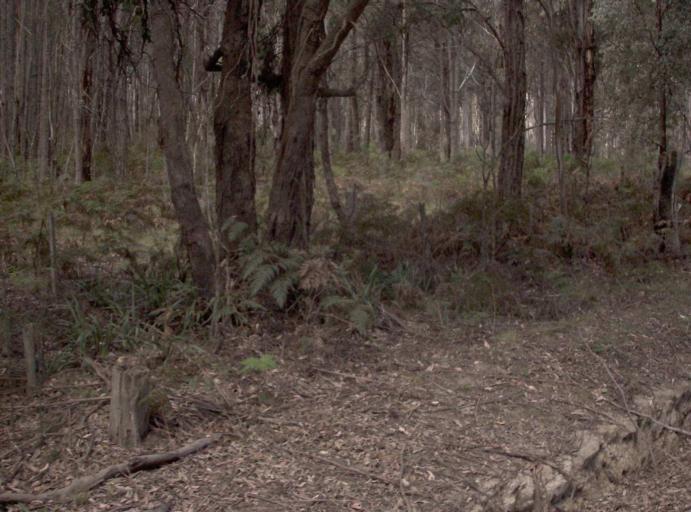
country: AU
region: New South Wales
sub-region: Bombala
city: Bombala
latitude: -37.1839
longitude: 148.7004
